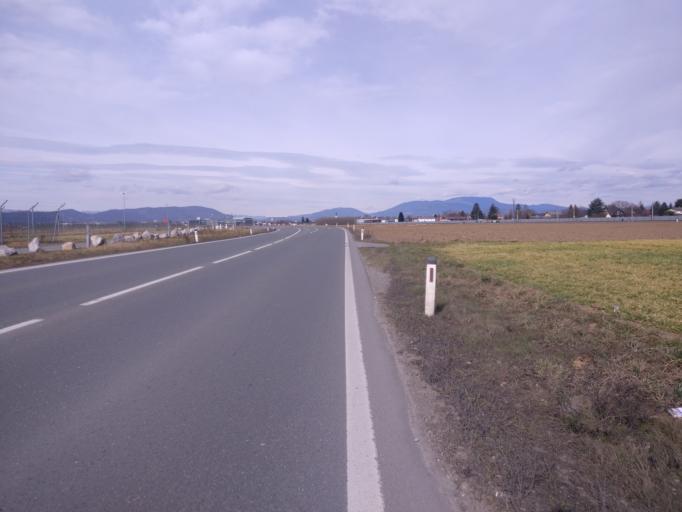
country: AT
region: Styria
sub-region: Politischer Bezirk Graz-Umgebung
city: Feldkirchen bei Graz
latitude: 46.9986
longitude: 15.4461
